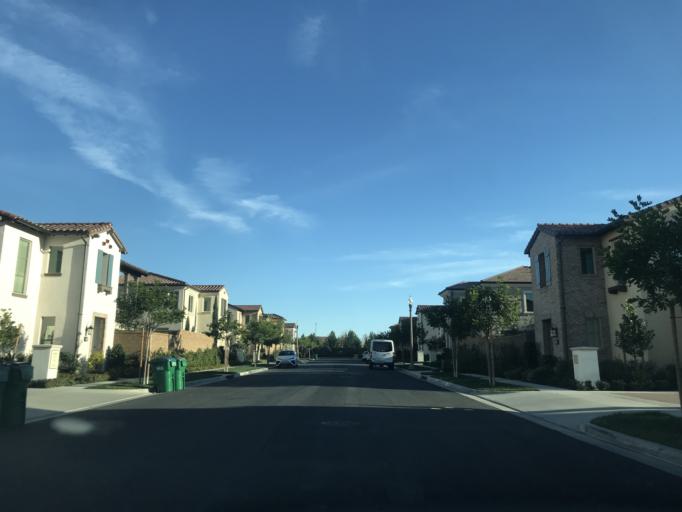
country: US
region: California
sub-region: Orange County
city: North Tustin
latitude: 33.7115
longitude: -117.7490
